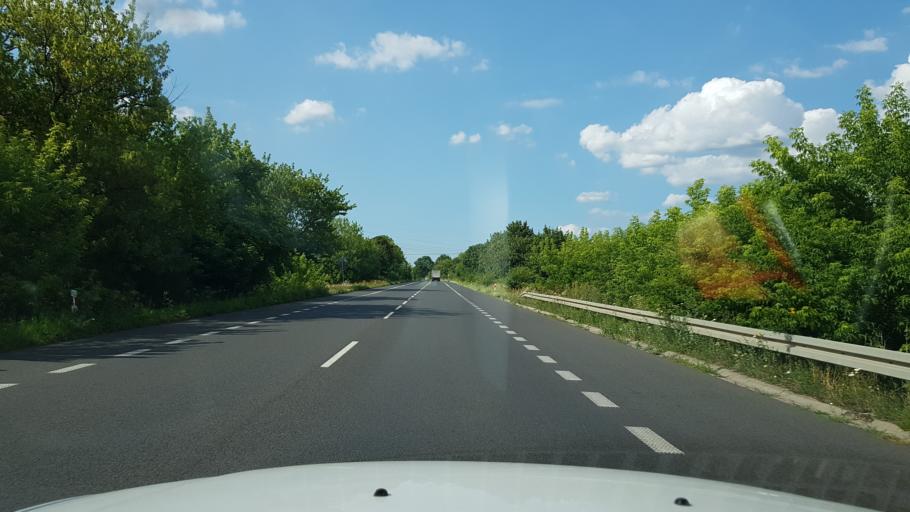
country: PL
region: West Pomeranian Voivodeship
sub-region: Powiat gryfinski
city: Stare Czarnowo
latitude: 53.2619
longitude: 14.7843
